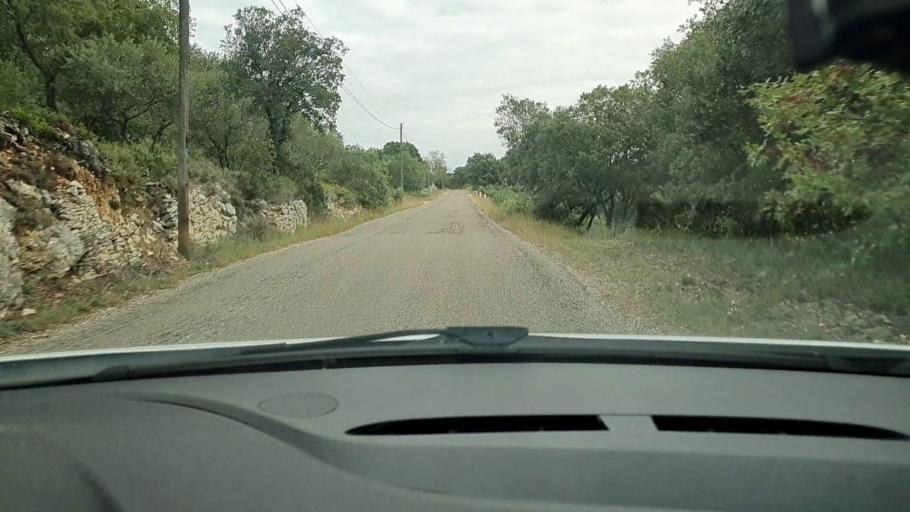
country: FR
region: Languedoc-Roussillon
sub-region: Departement du Gard
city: Montaren-et-Saint-Mediers
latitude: 44.0702
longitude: 4.3111
